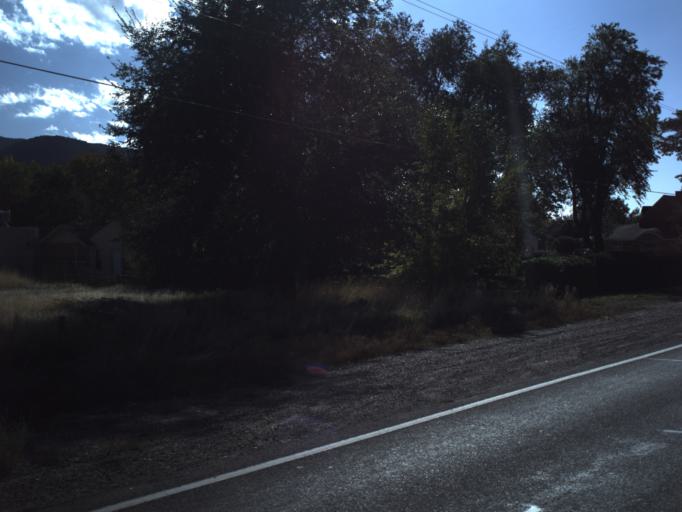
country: US
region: Utah
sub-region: Iron County
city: Parowan
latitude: 37.8389
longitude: -112.8332
